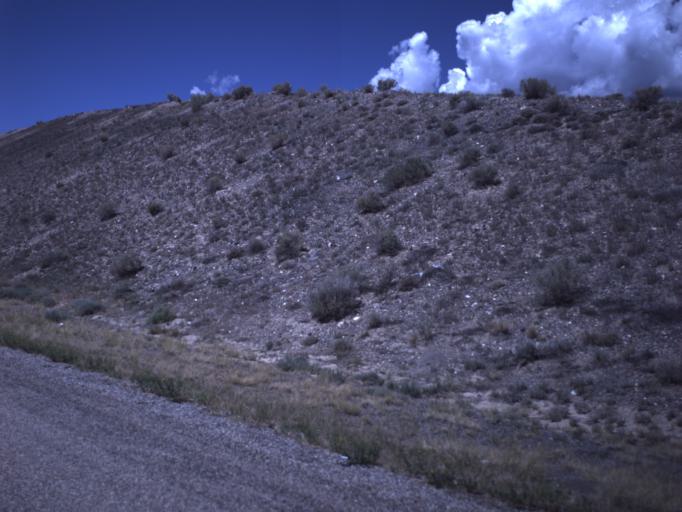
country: US
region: Utah
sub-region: Piute County
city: Junction
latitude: 38.2140
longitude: -112.2220
